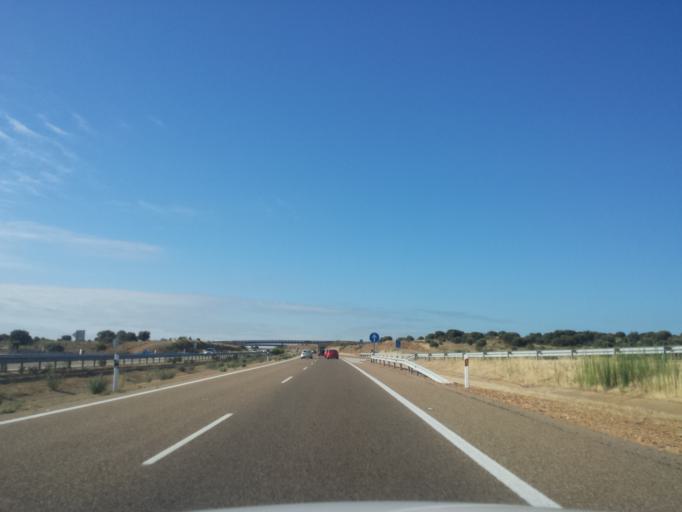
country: ES
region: Castille and Leon
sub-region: Provincia de Leon
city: Valdevimbre
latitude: 42.3982
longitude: -5.5953
